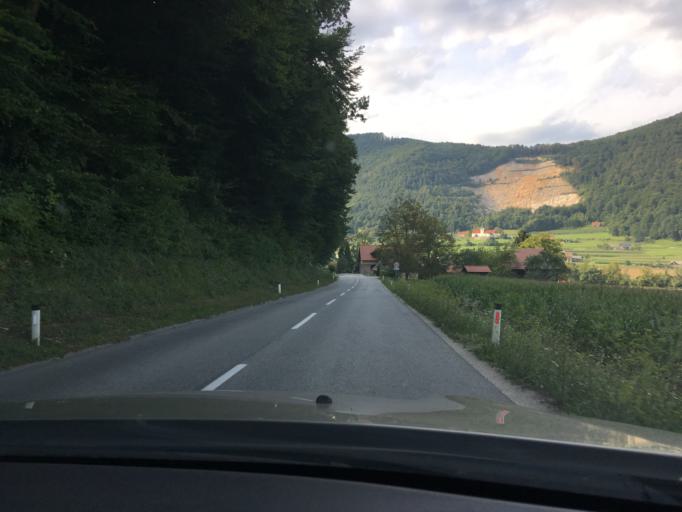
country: SI
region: Dolenjske Toplice
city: Dolenjske Toplice
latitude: 45.7725
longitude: 15.0227
